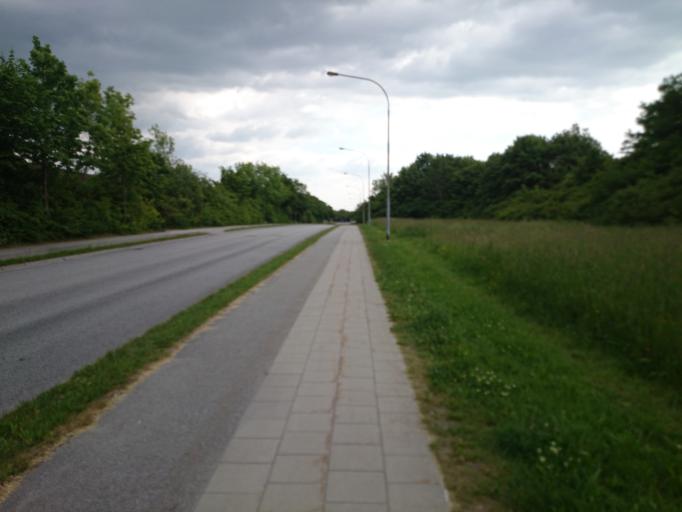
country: SE
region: Skane
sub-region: Lunds Kommun
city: Lund
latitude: 55.7128
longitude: 13.2229
